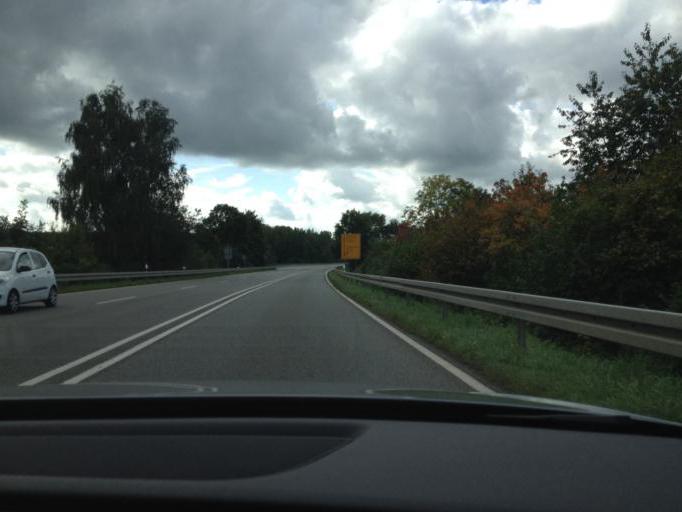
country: DE
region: Saarland
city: Sankt Wendel
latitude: 49.4879
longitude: 7.1507
